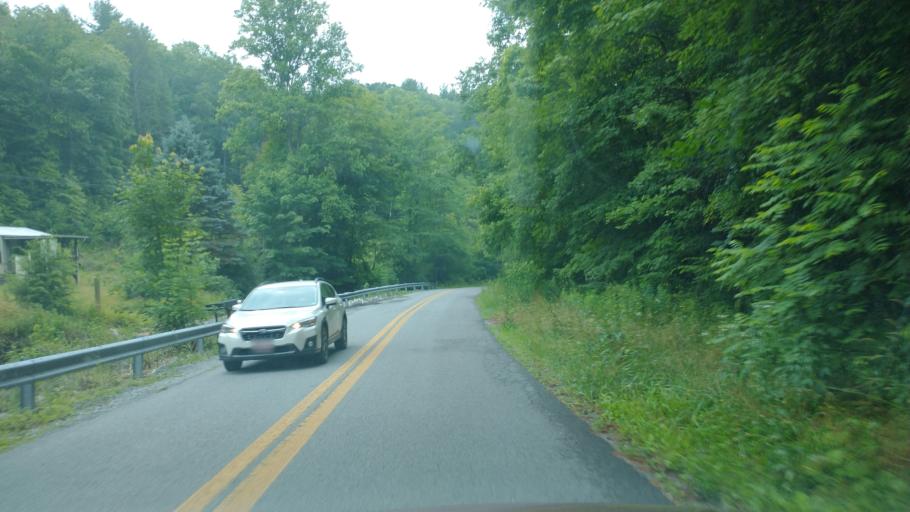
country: US
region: West Virginia
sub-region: Mercer County
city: Athens
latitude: 37.4324
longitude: -80.9763
